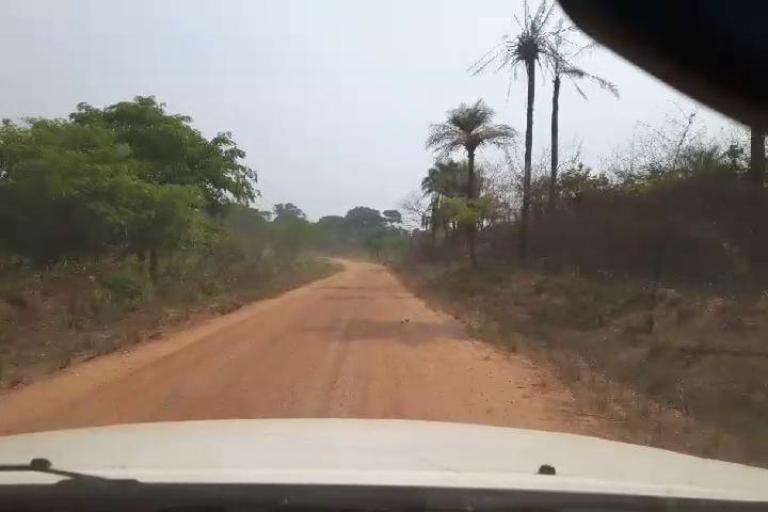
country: SL
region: Northern Province
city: Masingbi
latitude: 8.8817
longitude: -11.8200
